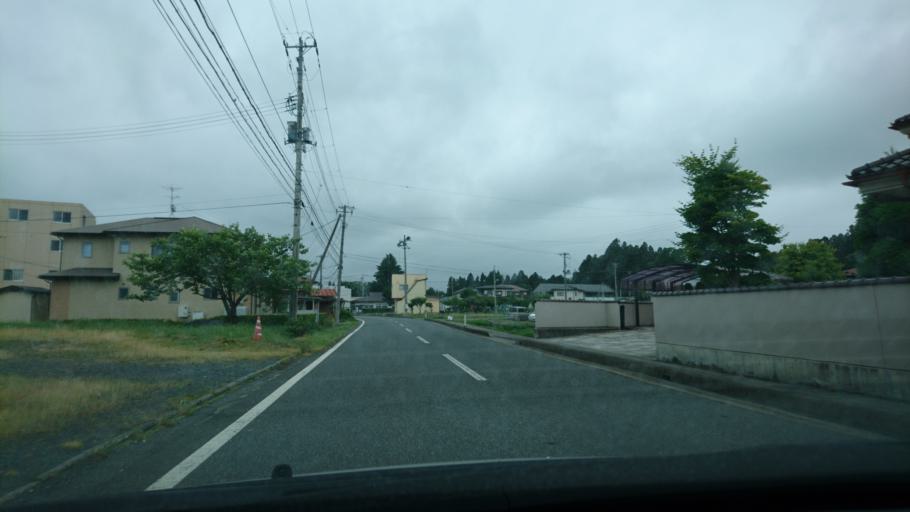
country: JP
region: Iwate
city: Ichinoseki
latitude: 38.9350
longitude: 141.0913
